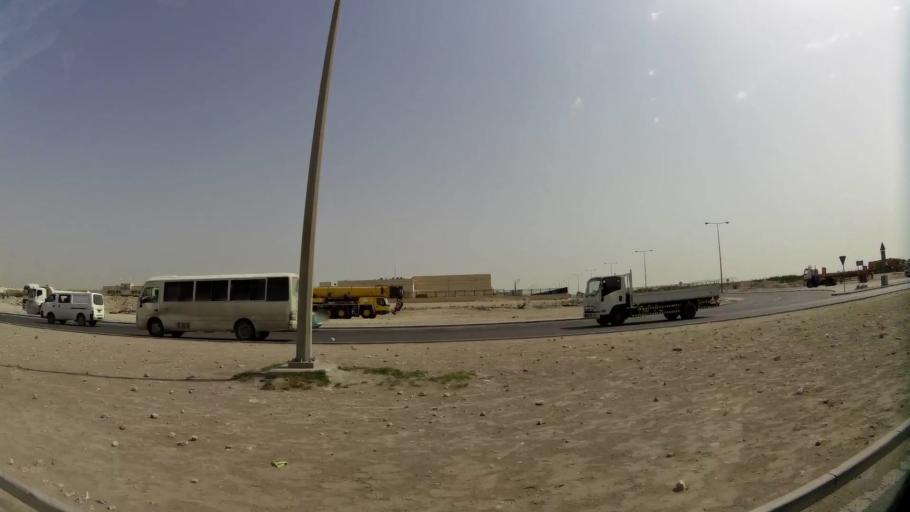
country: QA
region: Al Wakrah
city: Al Wukayr
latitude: 25.1830
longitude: 51.4619
